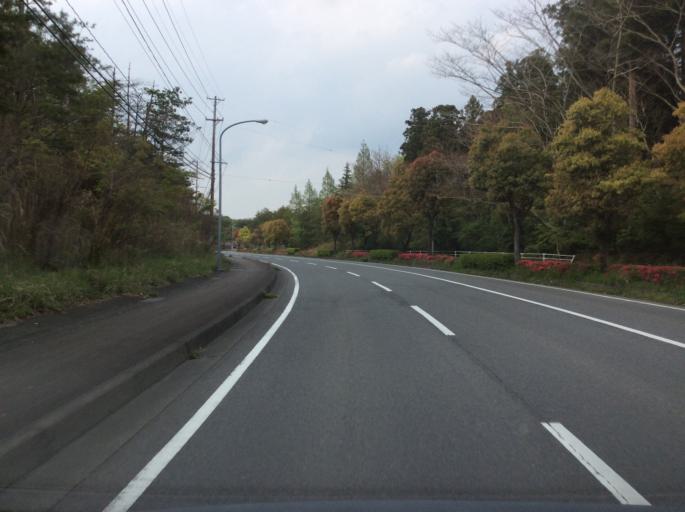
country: JP
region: Fukushima
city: Iwaki
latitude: 37.0739
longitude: 140.8437
